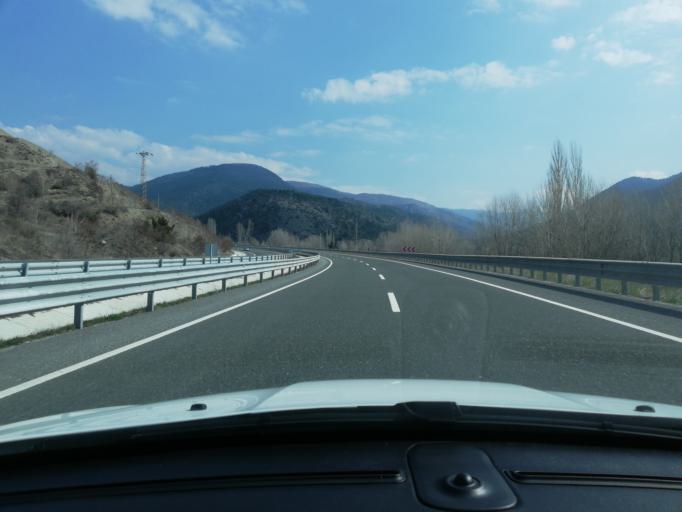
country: TR
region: Cankiri
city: Ilgaz
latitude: 40.9730
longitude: 33.6936
